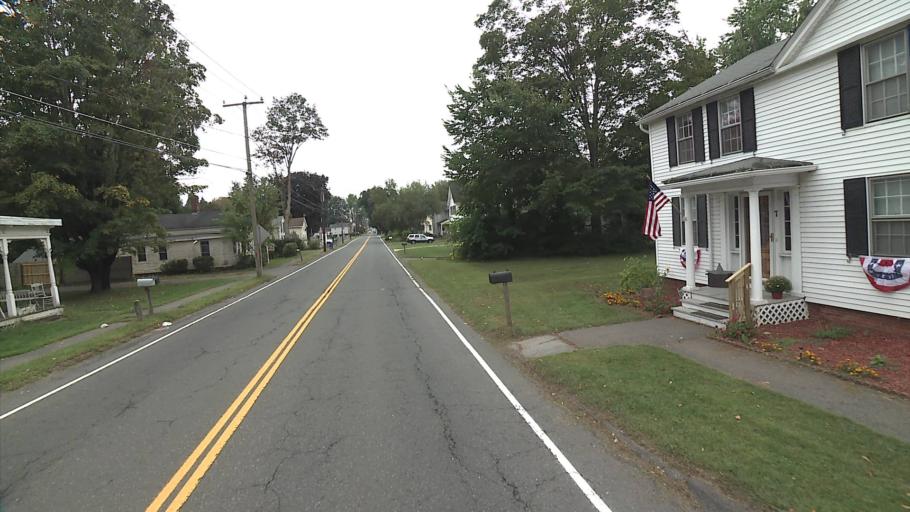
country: US
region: Connecticut
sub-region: Hartford County
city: Windsor Locks
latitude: 41.9345
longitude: -72.6177
